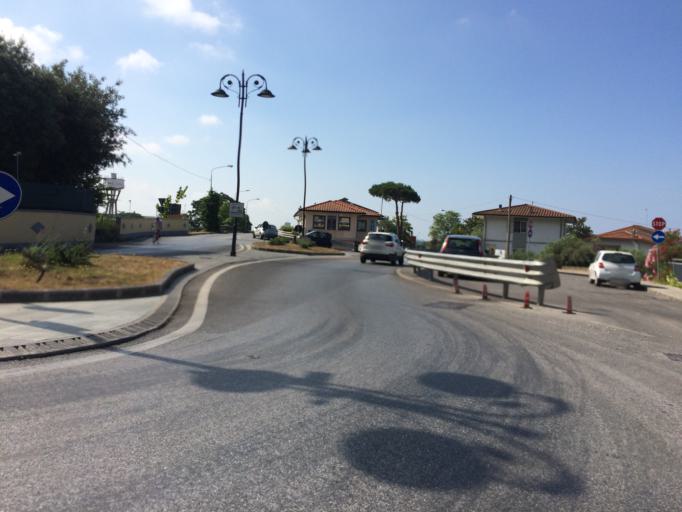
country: IT
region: Tuscany
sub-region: Provincia di Massa-Carrara
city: Capanne-Prato-Cinquale
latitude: 44.0085
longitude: 10.1600
